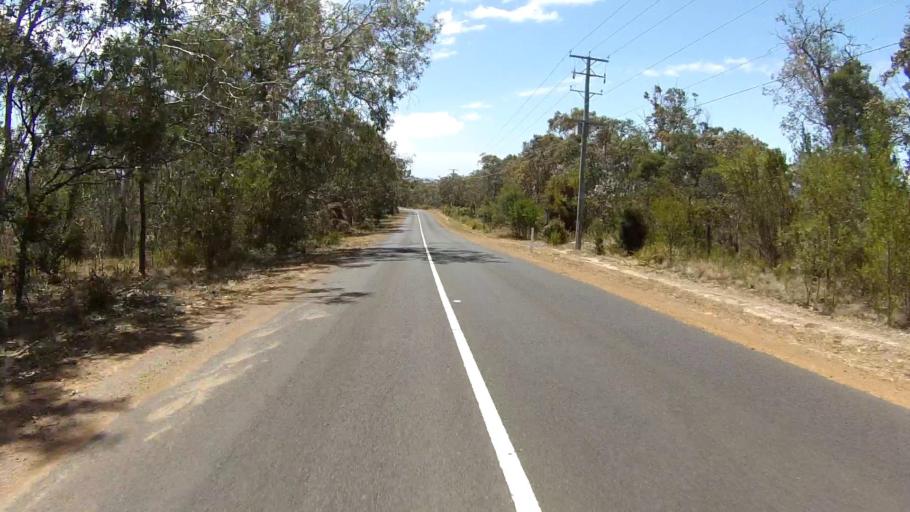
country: AU
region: Tasmania
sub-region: Clarence
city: Sandford
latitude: -43.0101
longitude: 147.4803
